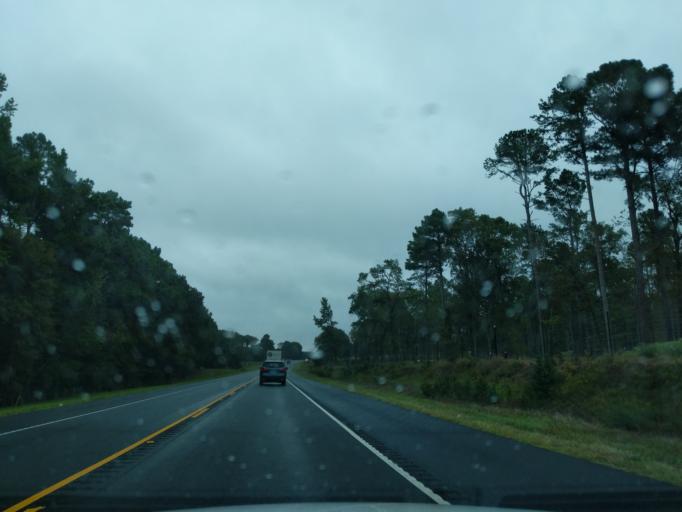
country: US
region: Louisiana
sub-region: Caddo Parish
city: Greenwood
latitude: 32.4322
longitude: -93.9844
